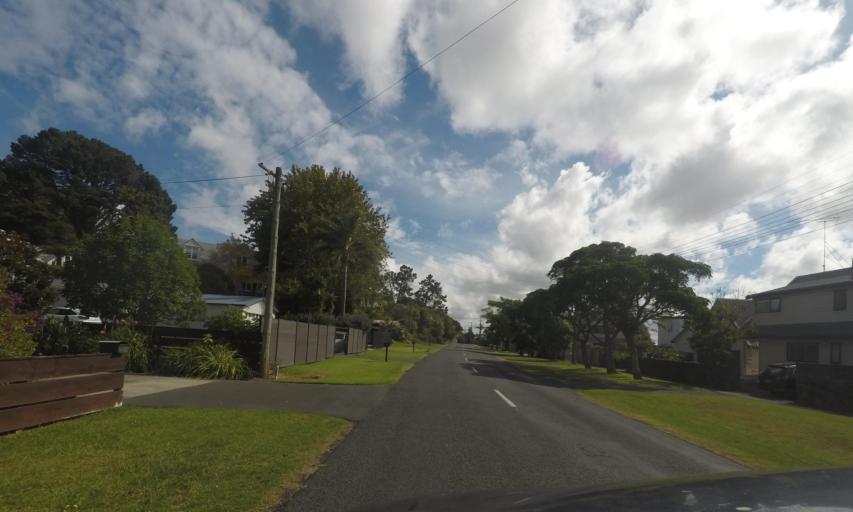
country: NZ
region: Auckland
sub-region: Auckland
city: North Shore
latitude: -36.7783
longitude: 174.6572
